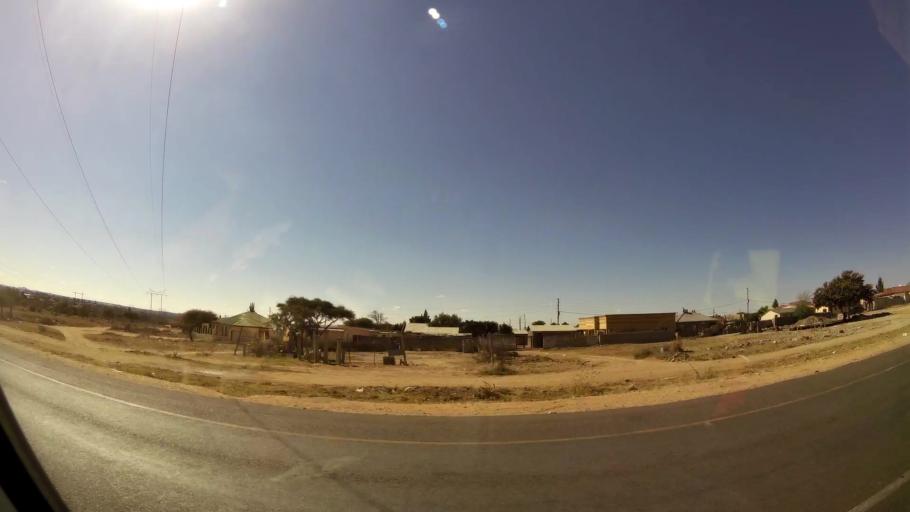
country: ZA
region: Limpopo
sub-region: Capricorn District Municipality
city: Polokwane
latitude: -23.8564
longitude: 29.4067
